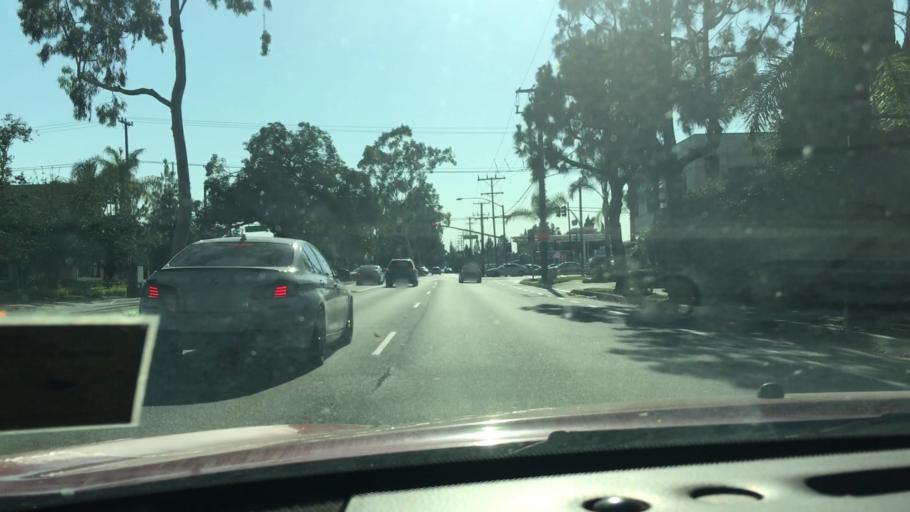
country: US
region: California
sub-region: Los Angeles County
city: Cerritos
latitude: 33.8733
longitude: -118.0455
